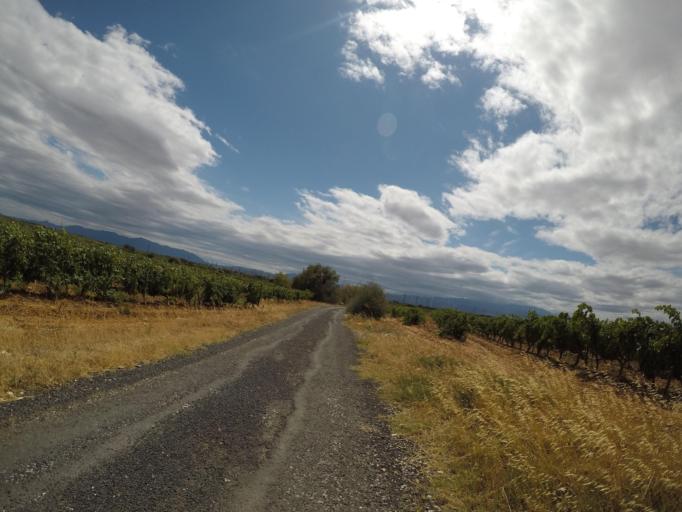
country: FR
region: Languedoc-Roussillon
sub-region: Departement des Pyrenees-Orientales
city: Baixas
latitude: 42.7412
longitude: 2.8048
